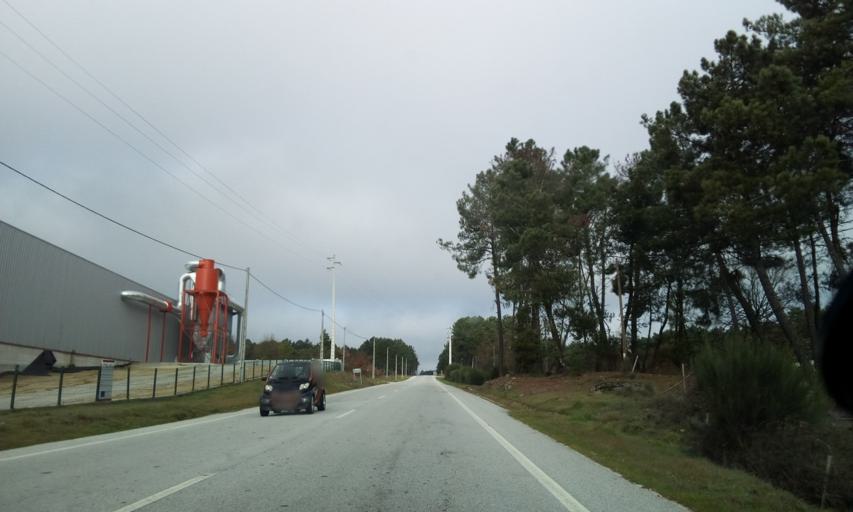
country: PT
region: Guarda
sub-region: Aguiar da Beira
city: Aguiar da Beira
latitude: 40.7924
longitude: -7.5122
